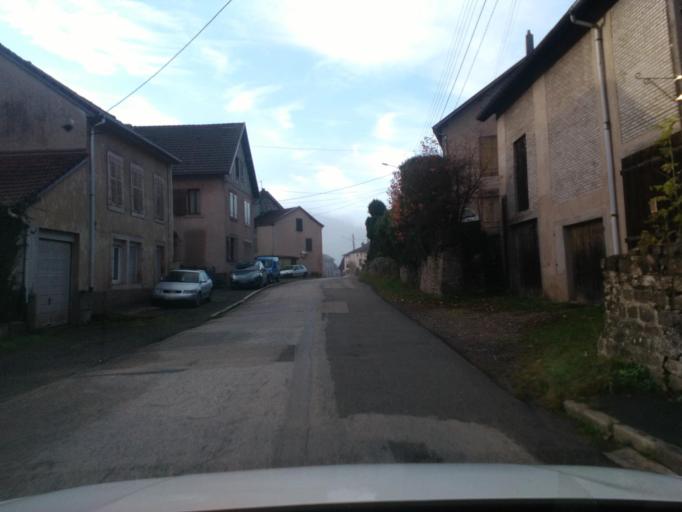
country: FR
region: Lorraine
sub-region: Departement des Vosges
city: Senones
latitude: 48.4270
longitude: 7.0181
